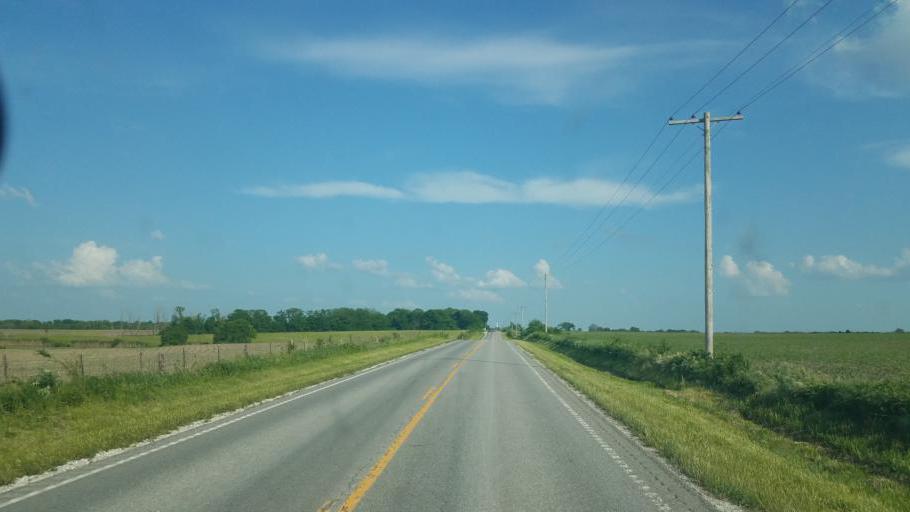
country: US
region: Missouri
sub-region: Cooper County
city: Boonville
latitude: 38.8301
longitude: -92.6122
